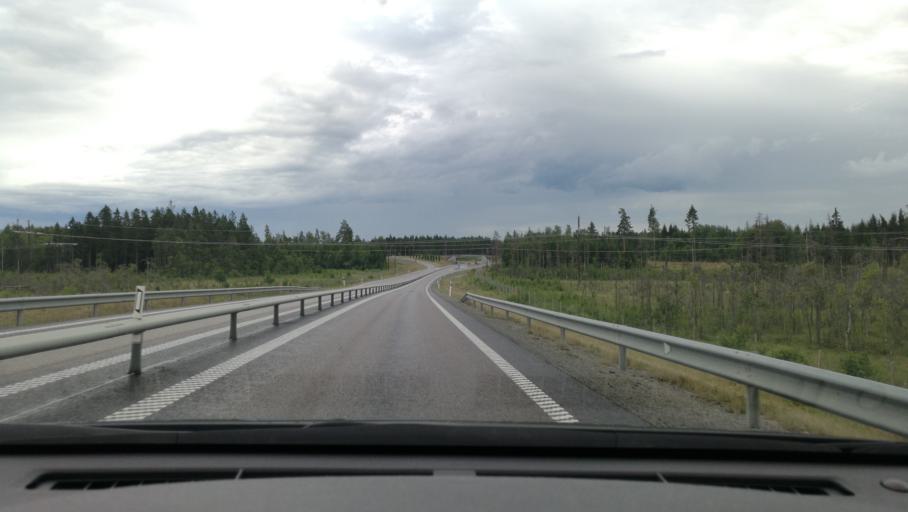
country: SE
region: Soedermanland
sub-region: Katrineholms Kommun
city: Katrineholm
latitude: 58.9981
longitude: 16.2540
